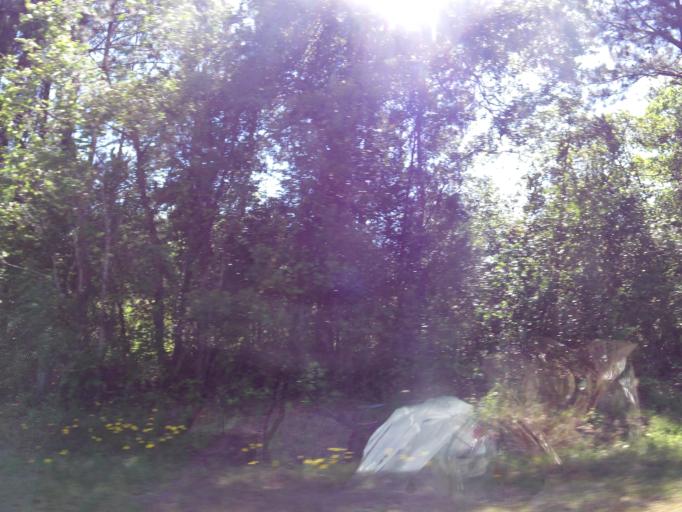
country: US
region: South Carolina
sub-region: Barnwell County
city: Williston
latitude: 33.4620
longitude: -81.4999
